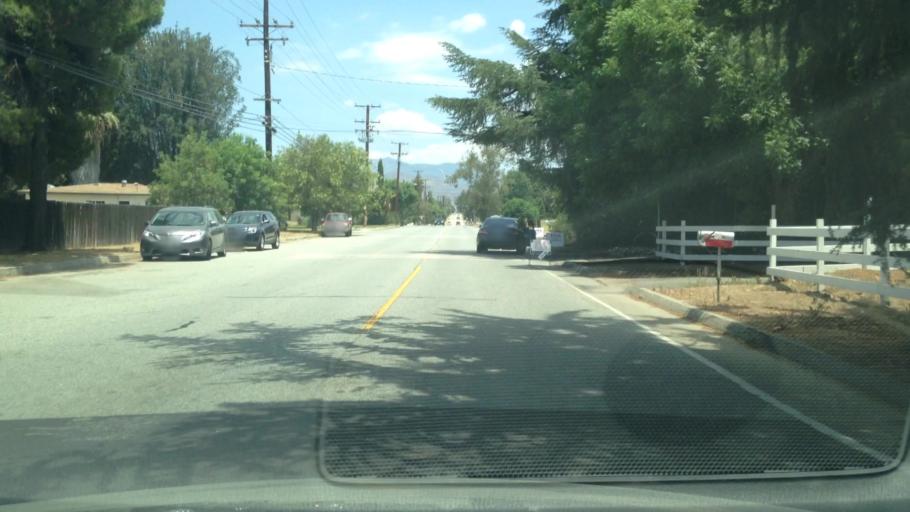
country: US
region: California
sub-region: San Bernardino County
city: Yucaipa
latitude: 34.0202
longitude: -117.0345
